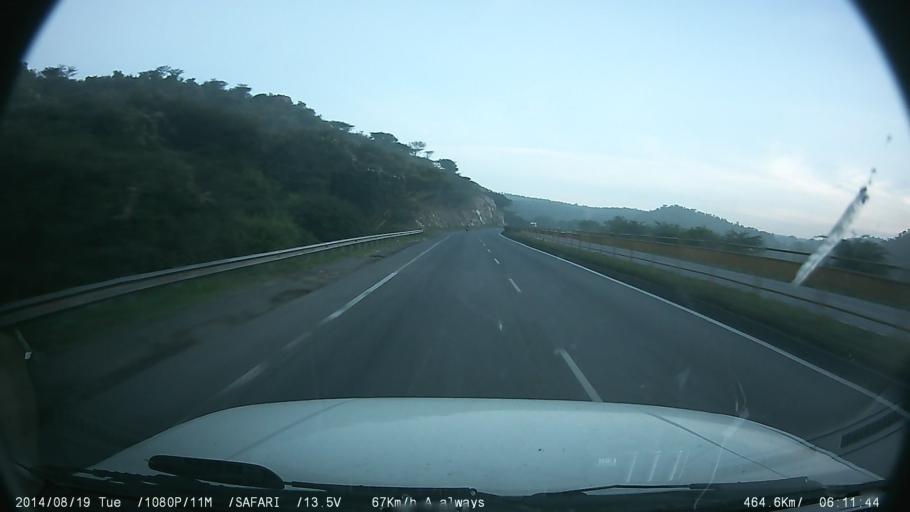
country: IN
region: Tamil Nadu
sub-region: Dharmapuri
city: Mallapuram
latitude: 11.9525
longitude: 78.0470
